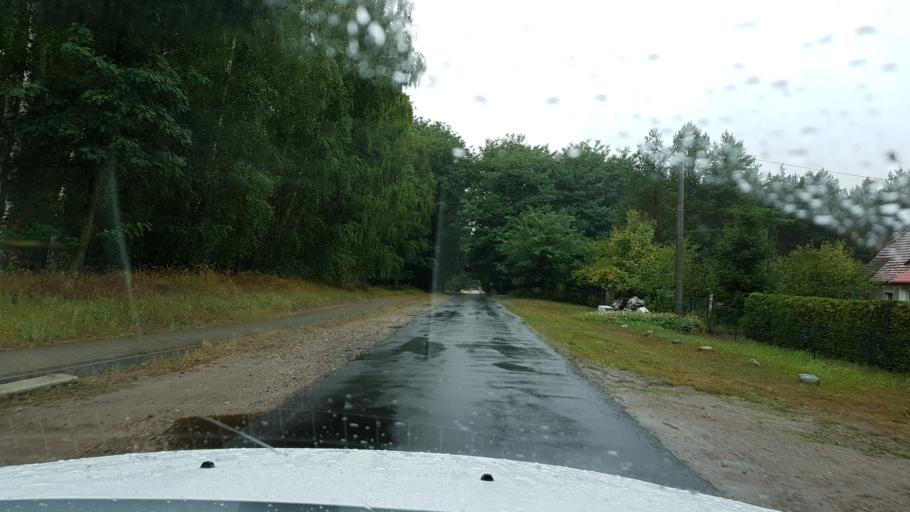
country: DE
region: Brandenburg
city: Meyenburg
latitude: 52.9773
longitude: 14.2192
